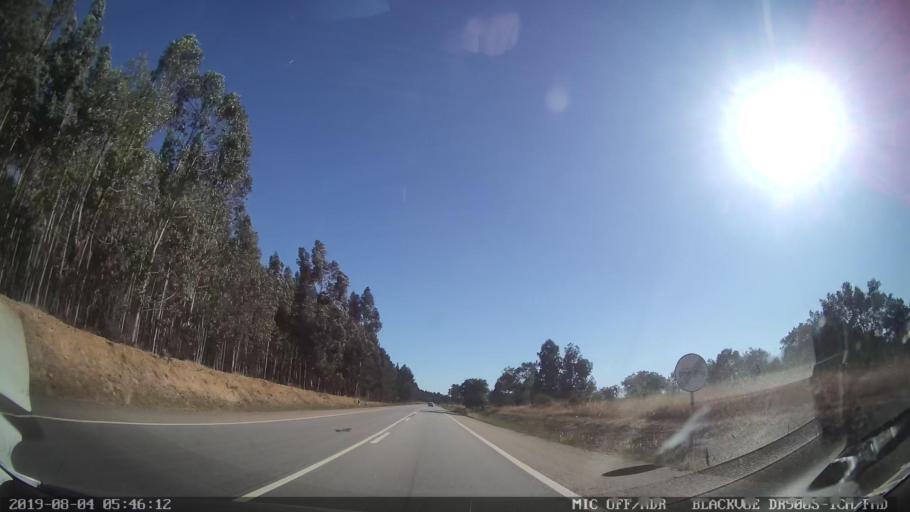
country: PT
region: Portalegre
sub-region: Gaviao
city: Gaviao
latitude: 39.4540
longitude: -7.7855
